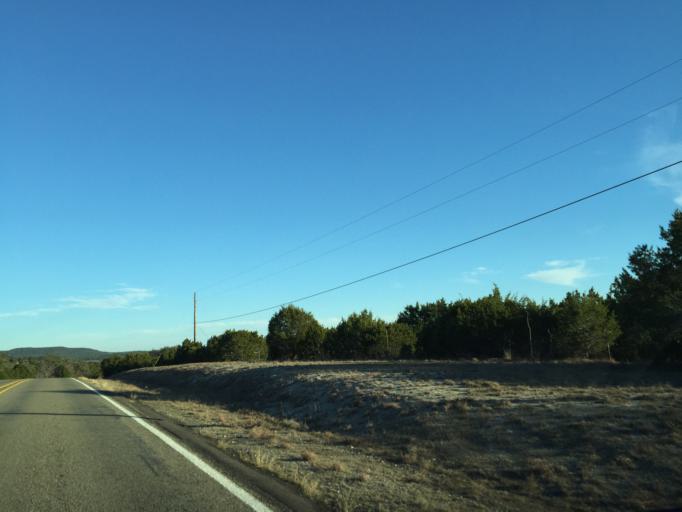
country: US
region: Texas
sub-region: Travis County
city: Lago Vista
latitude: 30.5216
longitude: -98.0490
